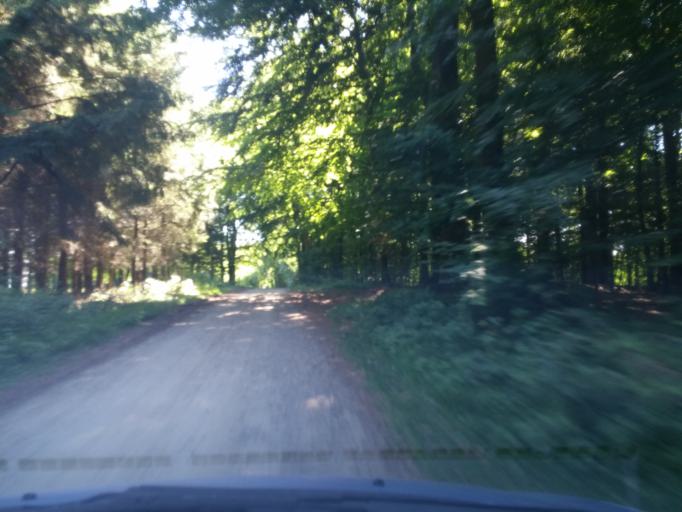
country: DK
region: South Denmark
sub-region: Aabenraa Kommune
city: Lojt Kirkeby
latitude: 55.1303
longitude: 9.5071
